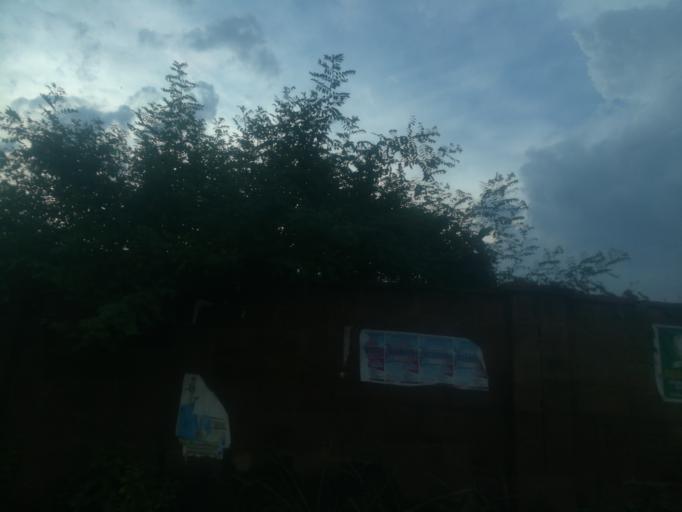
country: NG
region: Oyo
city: Ibadan
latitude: 7.3870
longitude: 3.8363
